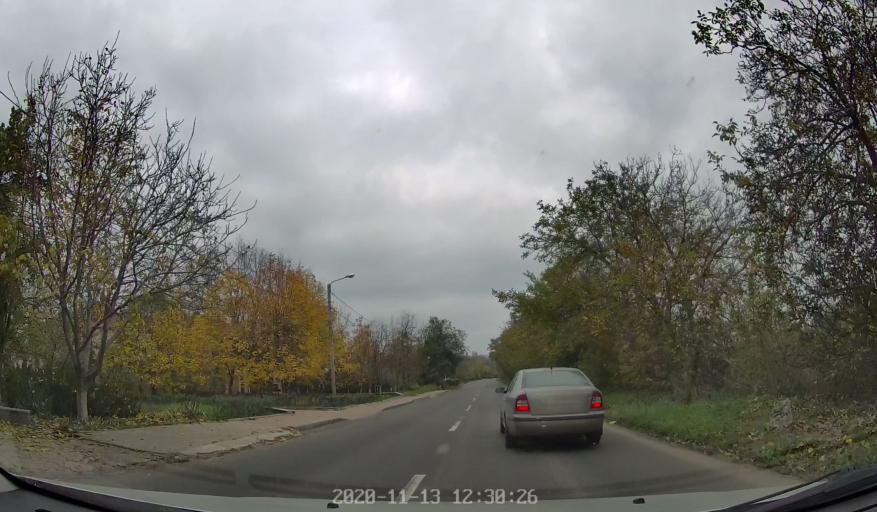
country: MD
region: Chisinau
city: Chisinau
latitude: 46.9693
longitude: 28.8336
